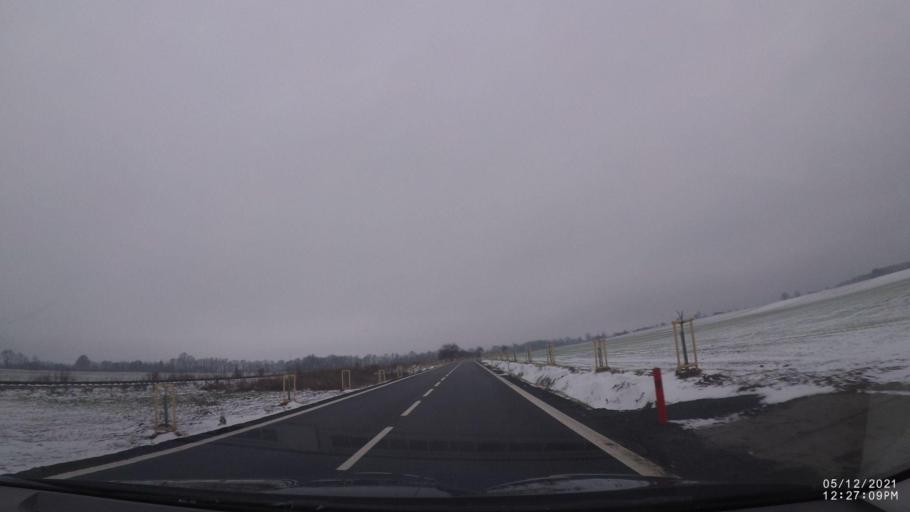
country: CZ
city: Nove Mesto nad Metuji
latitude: 50.3363
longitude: 16.1075
